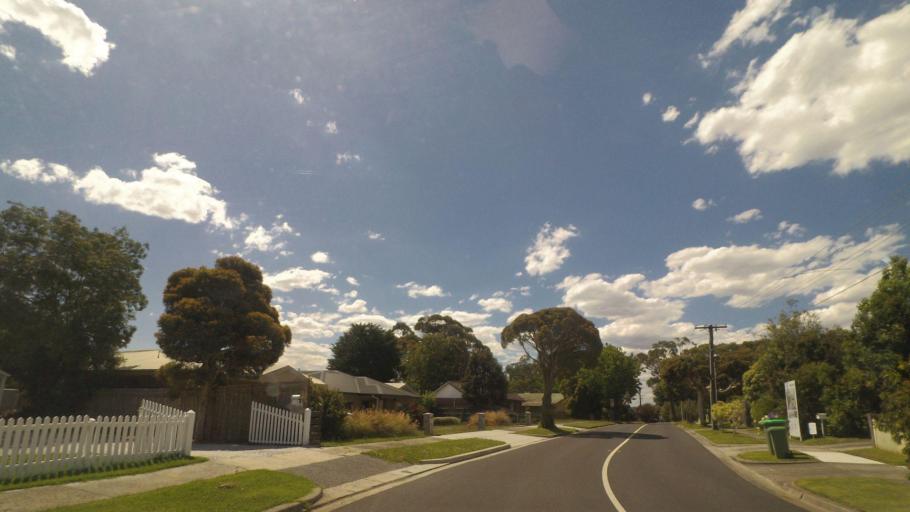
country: AU
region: Victoria
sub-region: Yarra Ranges
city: Kilsyth
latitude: -37.8058
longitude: 145.3201
